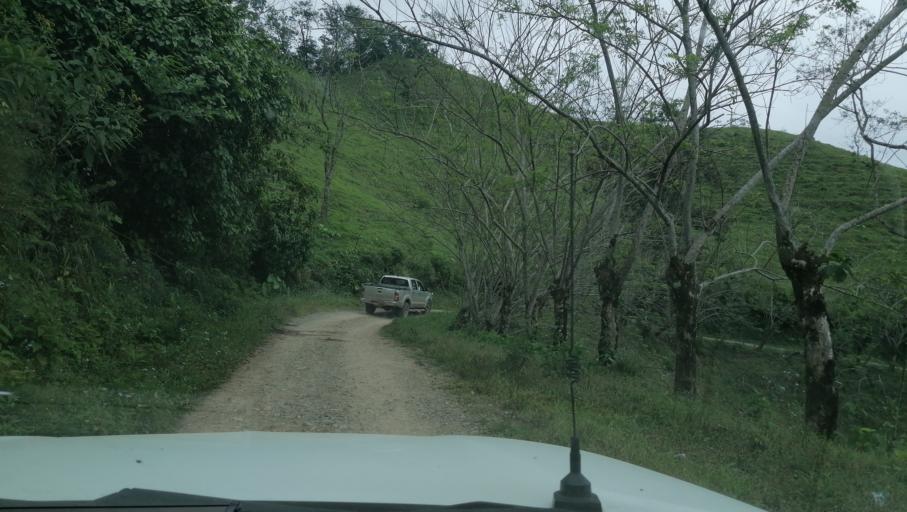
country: MX
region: Chiapas
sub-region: Francisco Leon
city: San Miguel la Sardina
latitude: 17.3421
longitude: -93.3100
